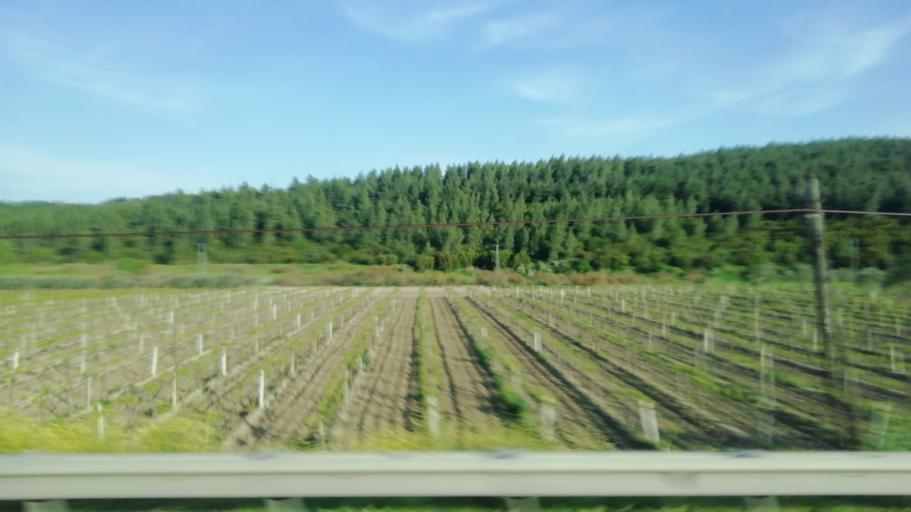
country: TR
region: Manisa
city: Halitpasa
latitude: 38.7921
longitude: 27.6808
